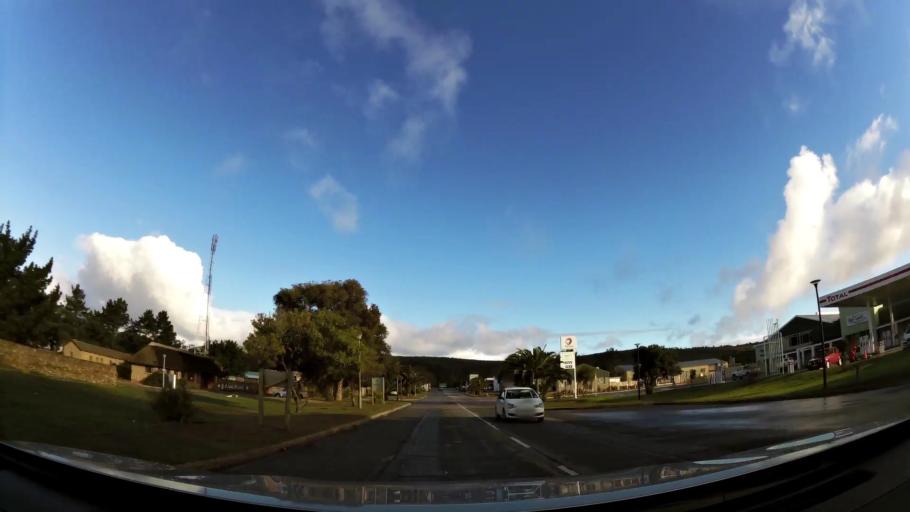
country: ZA
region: Western Cape
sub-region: Eden District Municipality
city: Riversdale
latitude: -34.2102
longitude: 21.5848
